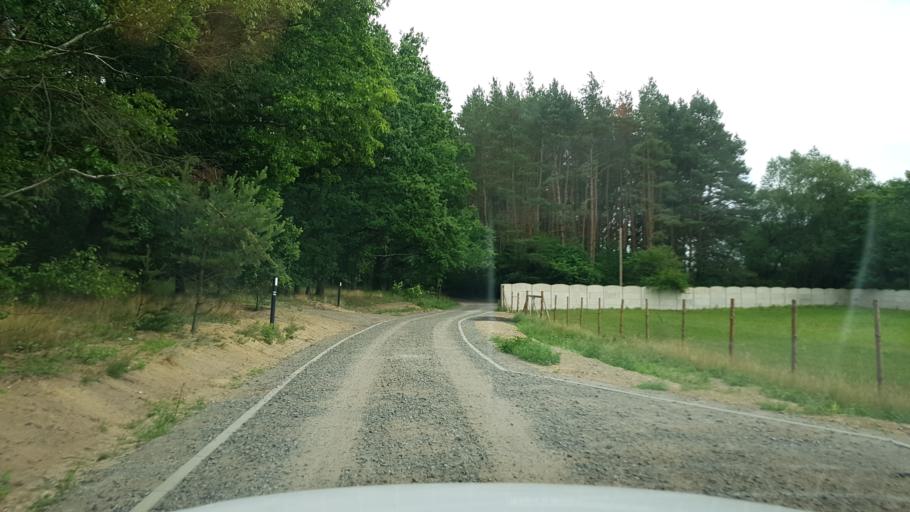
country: PL
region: West Pomeranian Voivodeship
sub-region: Powiat gryfinski
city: Stare Czarnowo
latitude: 53.3592
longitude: 14.7262
